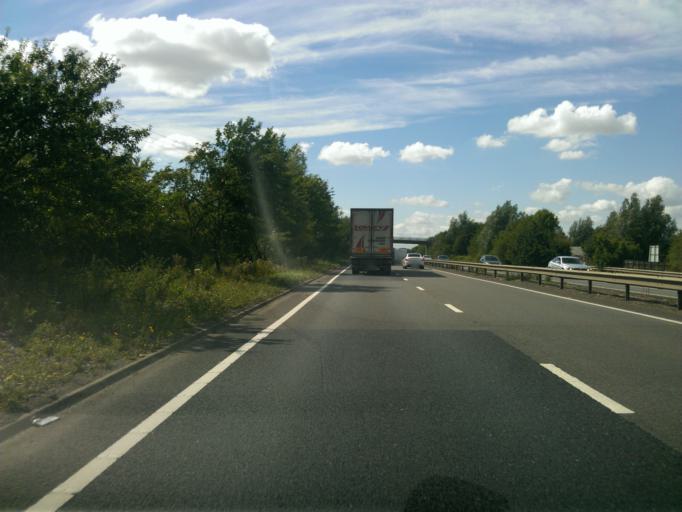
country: GB
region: England
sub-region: Cambridgeshire
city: Buckden
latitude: 52.3339
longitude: -0.2945
